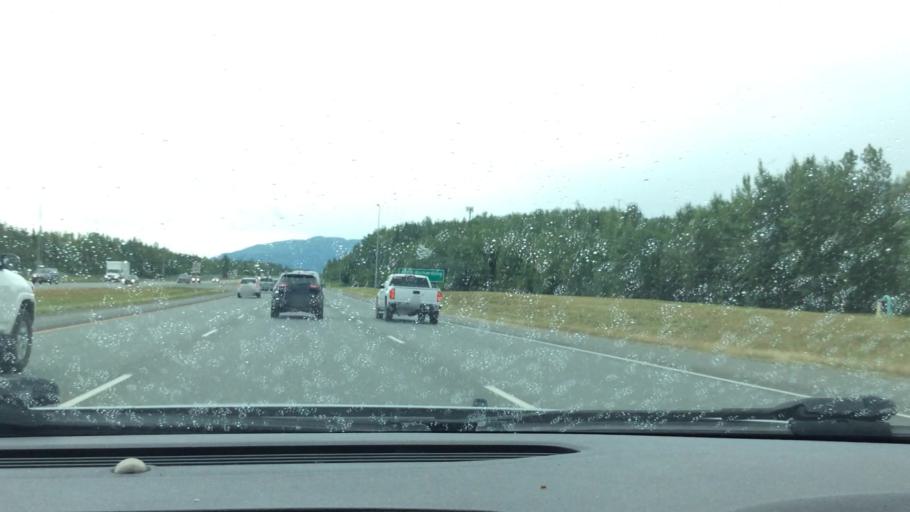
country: US
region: Alaska
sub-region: Anchorage Municipality
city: Elmendorf Air Force Base
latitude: 61.2398
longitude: -149.6899
